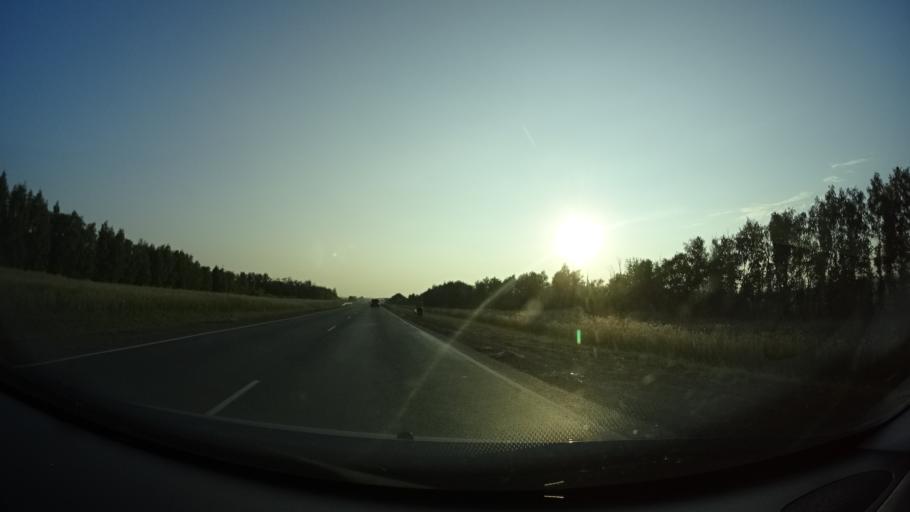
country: RU
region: Samara
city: Klyavlino
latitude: 54.0235
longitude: 51.8562
